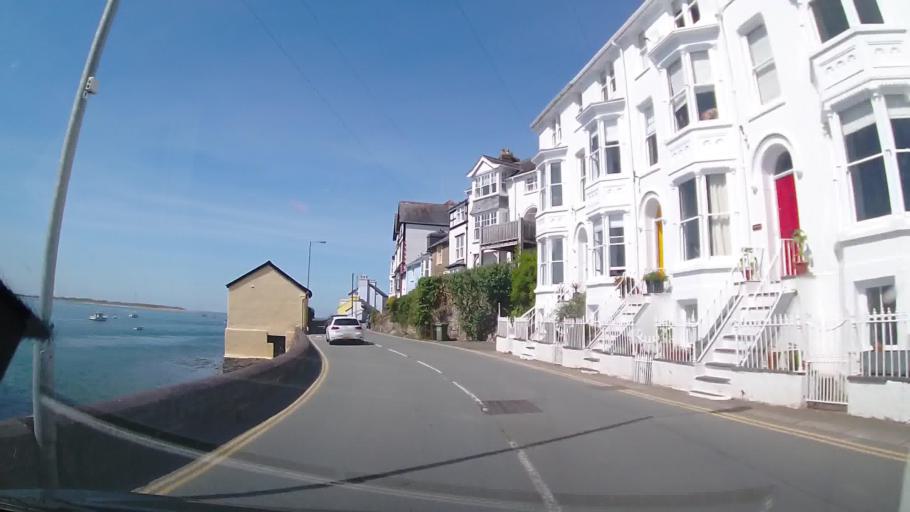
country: GB
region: Wales
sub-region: Gwynedd
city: Tywyn
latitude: 52.5449
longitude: -4.0387
